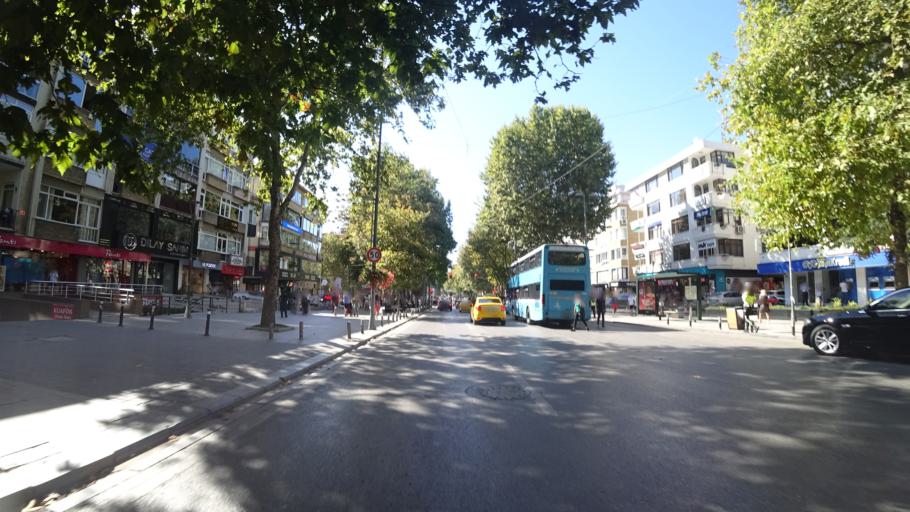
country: TR
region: Istanbul
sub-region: Atasehir
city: Atasehir
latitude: 40.9630
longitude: 29.0756
